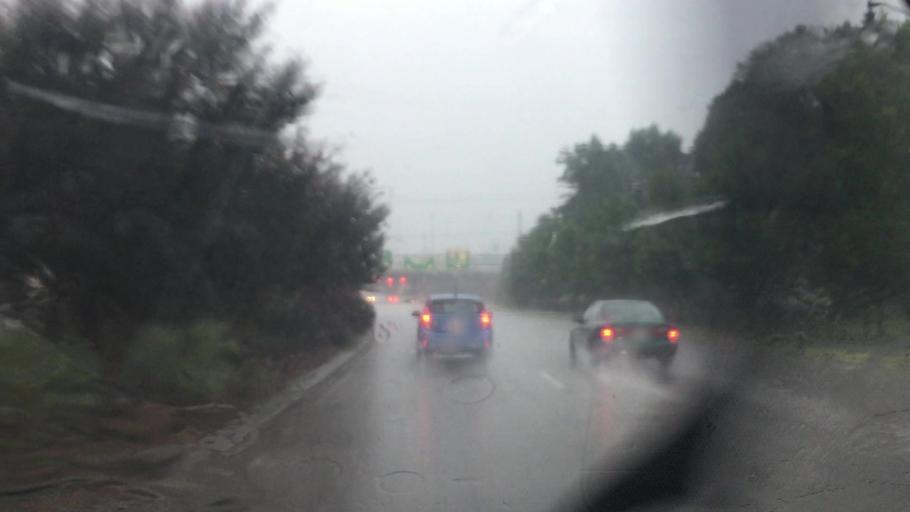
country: US
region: North Carolina
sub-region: Rowan County
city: Salisbury
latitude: 35.6555
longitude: -80.4578
